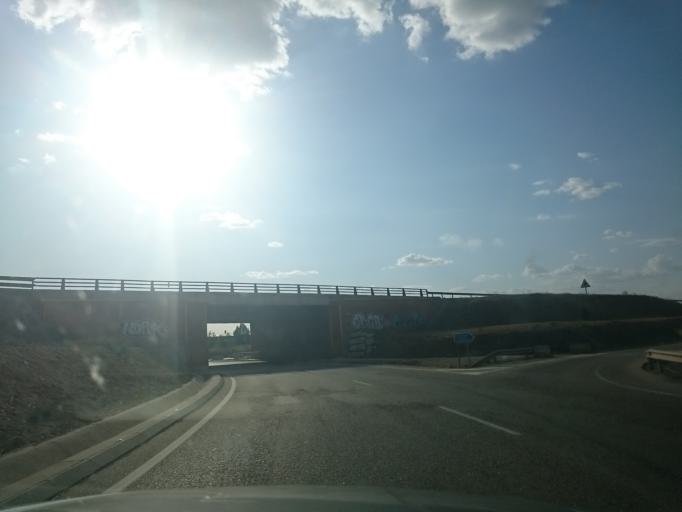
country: ES
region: Castille and Leon
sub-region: Provincia de Burgos
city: Cardenajimeno
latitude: 42.3450
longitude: -3.6372
